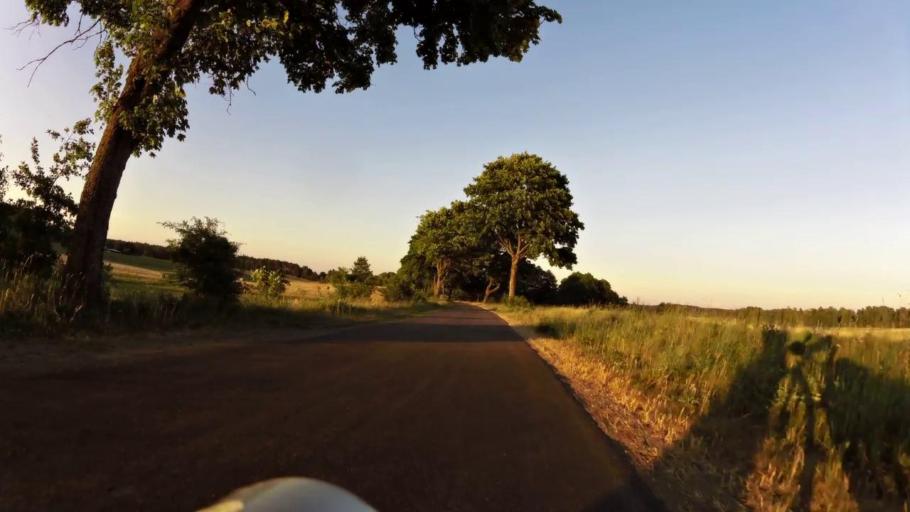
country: PL
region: West Pomeranian Voivodeship
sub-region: Powiat szczecinecki
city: Bialy Bor
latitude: 53.8614
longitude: 16.7350
